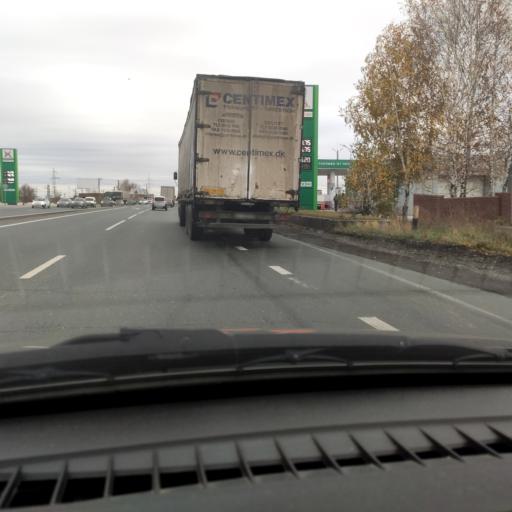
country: RU
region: Samara
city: Tol'yatti
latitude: 53.5774
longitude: 49.4002
